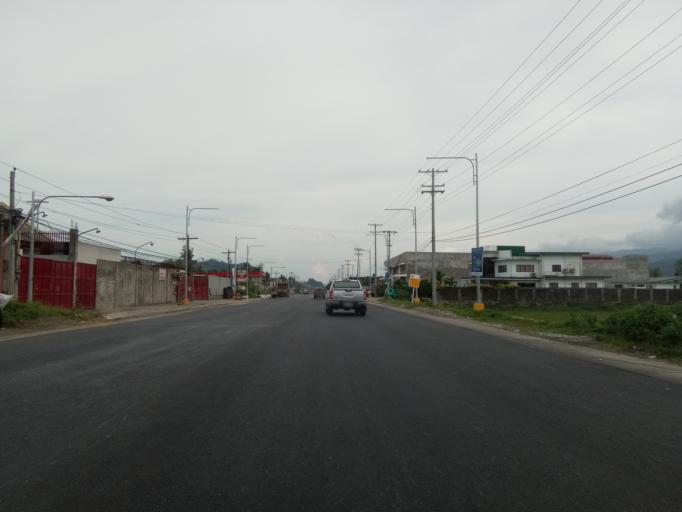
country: PH
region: Caraga
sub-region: Province of Surigao del Norte
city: Rizal
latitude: 9.7710
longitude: 125.4834
